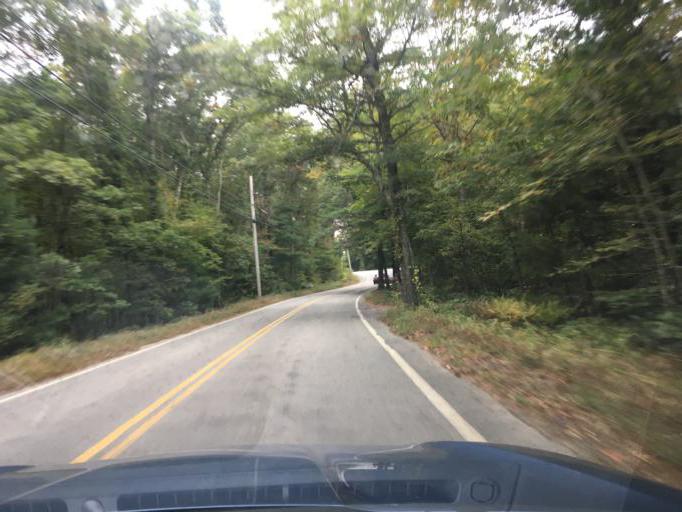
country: US
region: Rhode Island
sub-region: Washington County
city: Exeter
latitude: 41.6169
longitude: -71.5644
